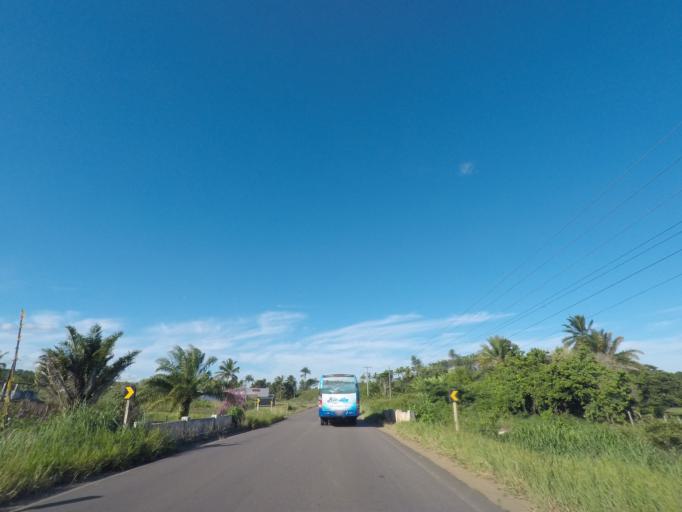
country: BR
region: Bahia
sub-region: Nazare
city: Nazare
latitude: -13.0560
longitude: -39.0059
